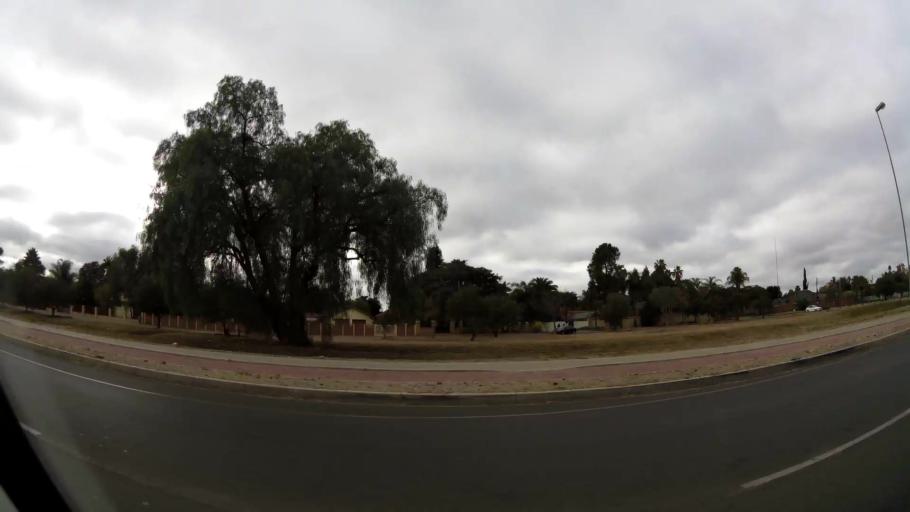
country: ZA
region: Limpopo
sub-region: Capricorn District Municipality
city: Polokwane
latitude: -23.9274
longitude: 29.4512
